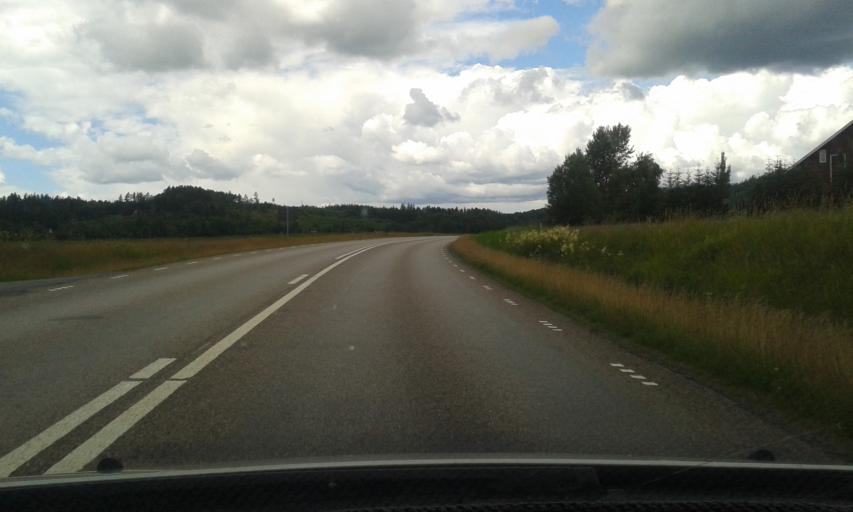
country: SE
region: Vaestra Goetaland
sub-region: Lilla Edets Kommun
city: Lilla Edet
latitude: 58.1355
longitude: 12.1025
